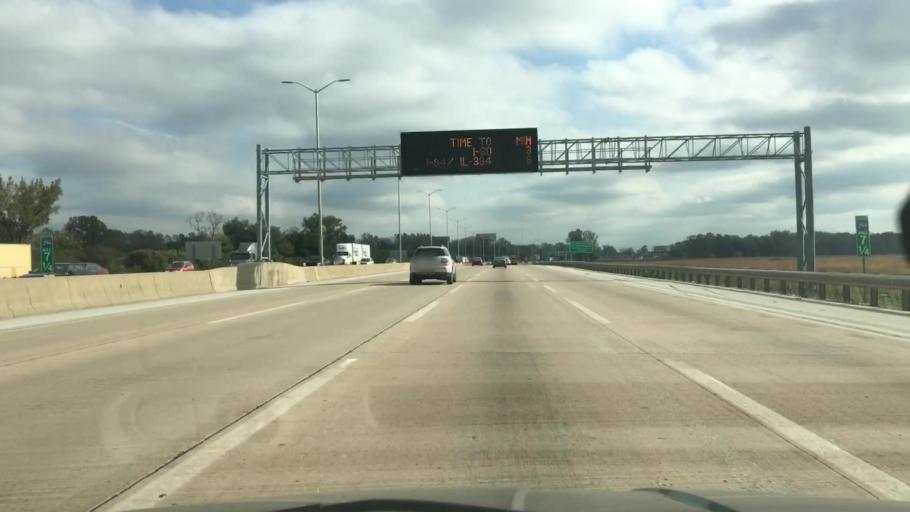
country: US
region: Illinois
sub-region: Cook County
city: Posen
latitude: 41.6133
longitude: -87.6845
